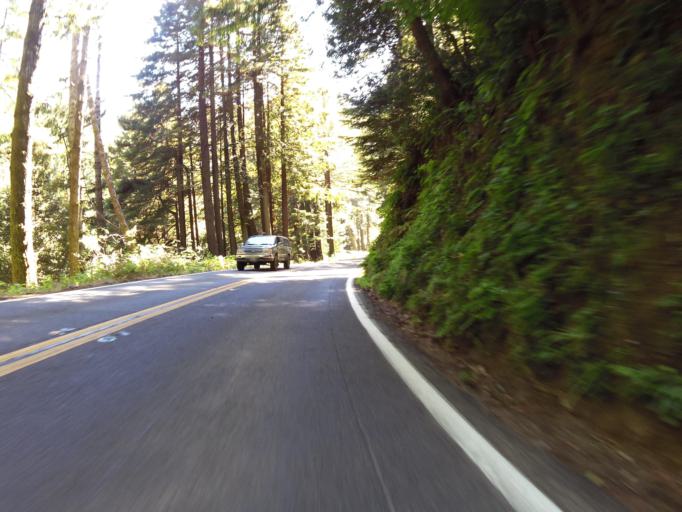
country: US
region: California
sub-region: Mendocino County
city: Fort Bragg
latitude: 39.7163
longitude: -123.8002
